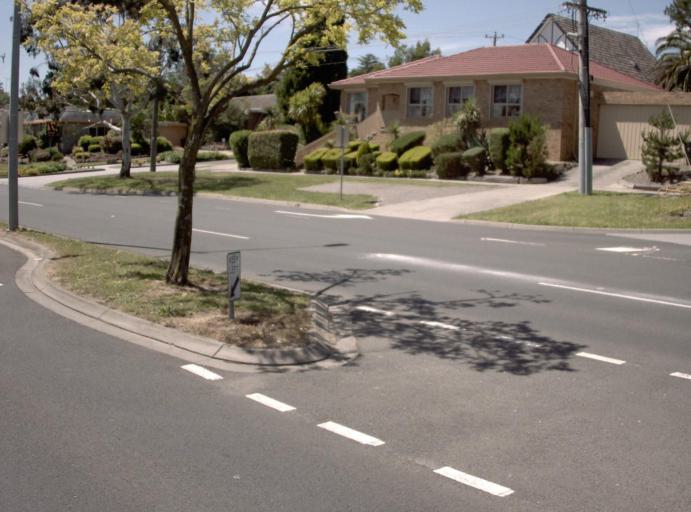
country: AU
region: Victoria
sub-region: Manningham
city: Donvale
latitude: -37.7808
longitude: 145.1634
